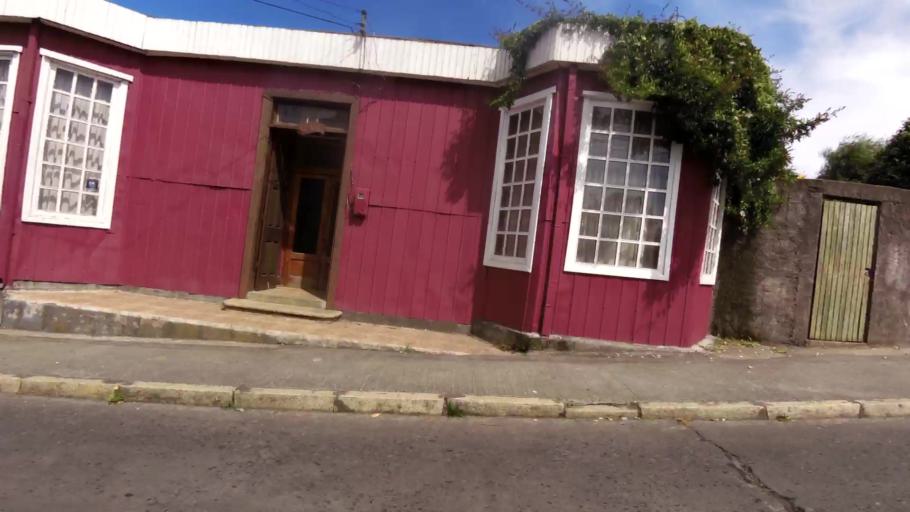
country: CL
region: Biobio
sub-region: Provincia de Concepcion
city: Talcahuano
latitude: -36.7186
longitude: -73.1109
